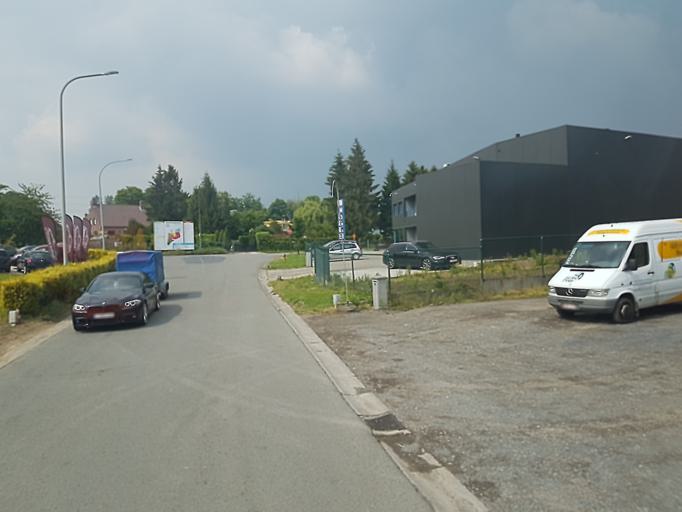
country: BE
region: Flanders
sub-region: Provincie Oost-Vlaanderen
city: Geraardsbergen
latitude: 50.7933
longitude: 3.8765
